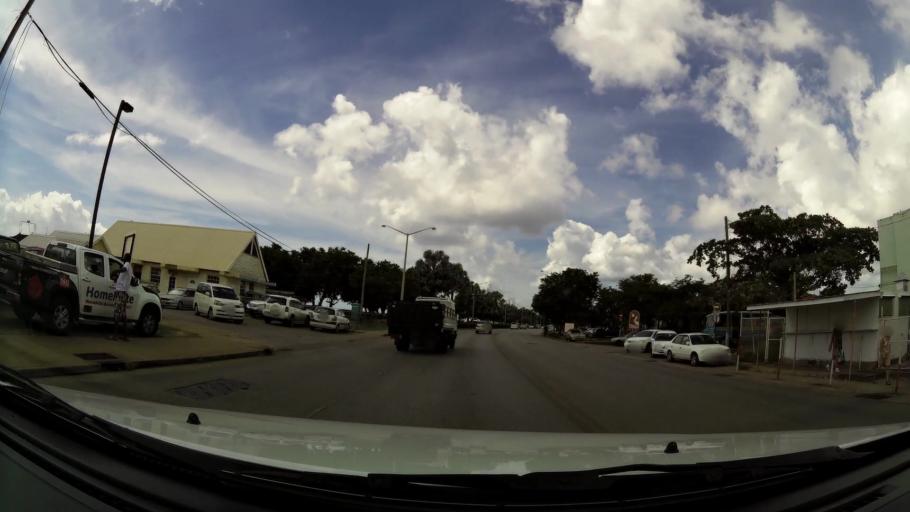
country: BB
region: Saint Michael
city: Bridgetown
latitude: 13.0975
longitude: -59.6220
